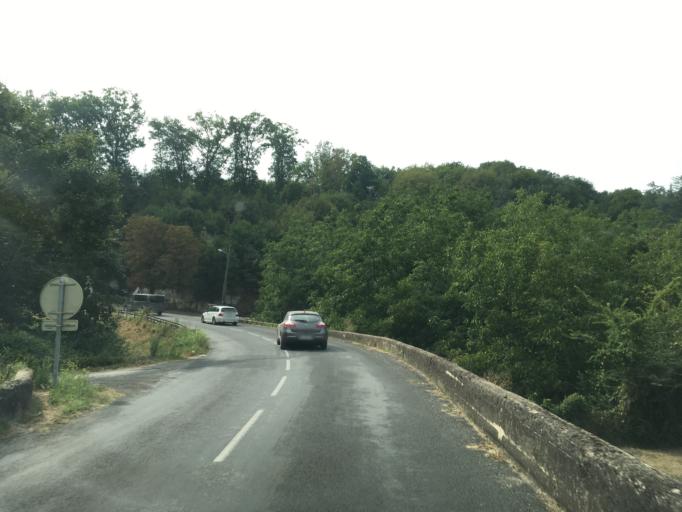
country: FR
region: Midi-Pyrenees
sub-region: Departement du Lot
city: Souillac
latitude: 44.8536
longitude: 1.5225
